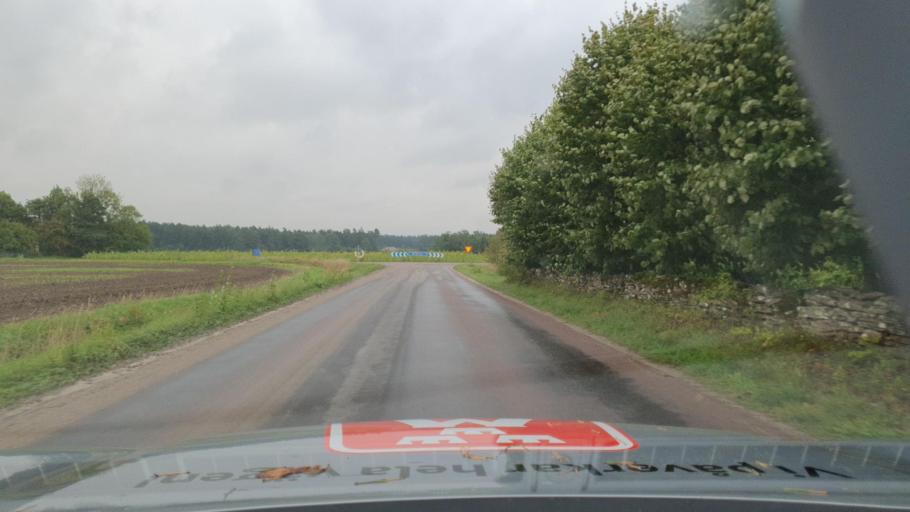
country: SE
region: Gotland
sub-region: Gotland
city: Slite
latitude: 57.6429
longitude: 18.5539
